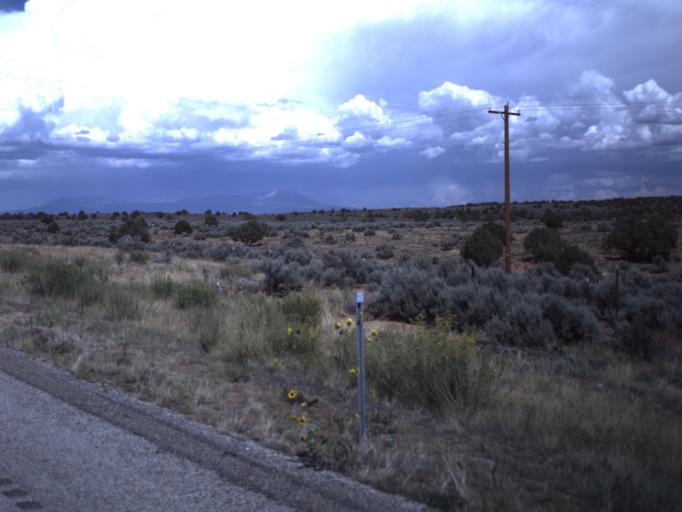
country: US
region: Utah
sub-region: San Juan County
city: Blanding
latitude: 37.4901
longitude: -109.4788
